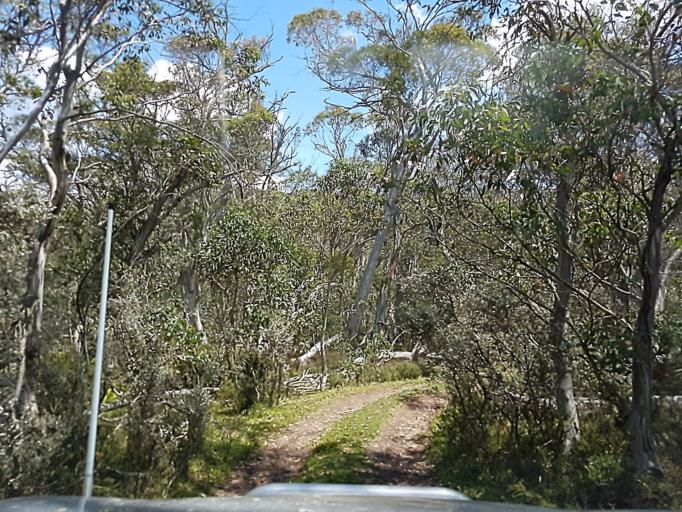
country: AU
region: New South Wales
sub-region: Snowy River
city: Jindabyne
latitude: -36.9036
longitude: 148.1289
